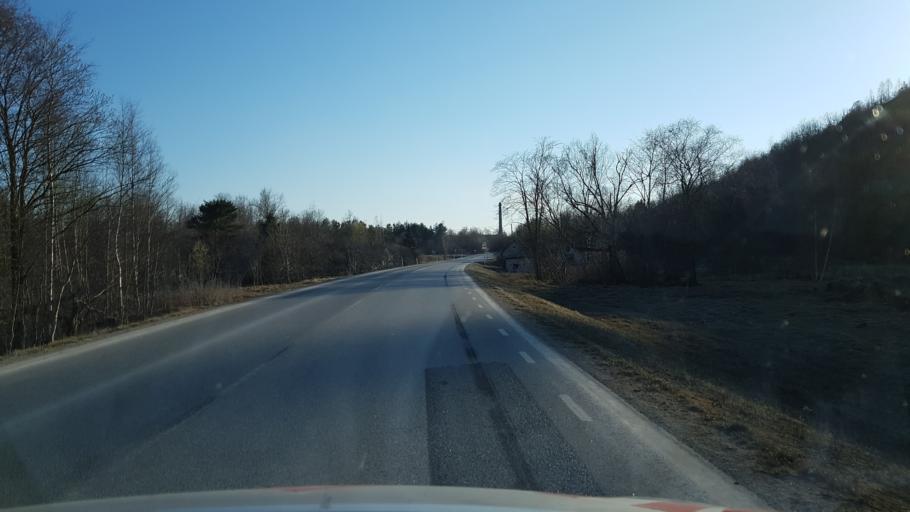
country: EE
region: Ida-Virumaa
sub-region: Kivioli linn
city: Kivioli
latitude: 59.3613
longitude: 26.9593
